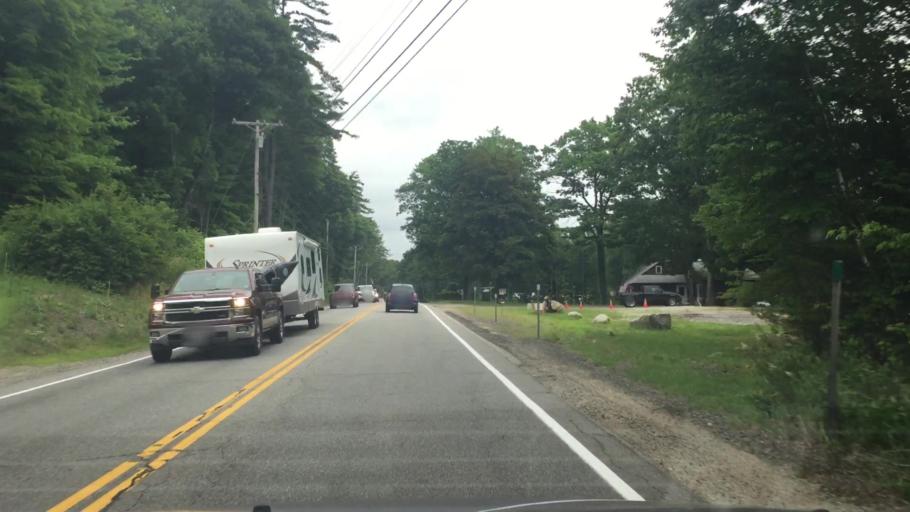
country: US
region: New Hampshire
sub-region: Carroll County
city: Moultonborough
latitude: 43.7366
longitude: -71.4142
